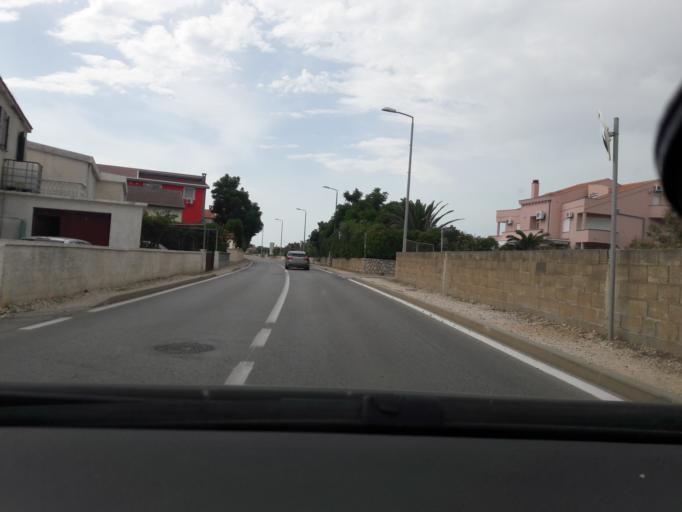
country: HR
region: Zadarska
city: Privlaka
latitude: 44.2936
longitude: 15.1185
